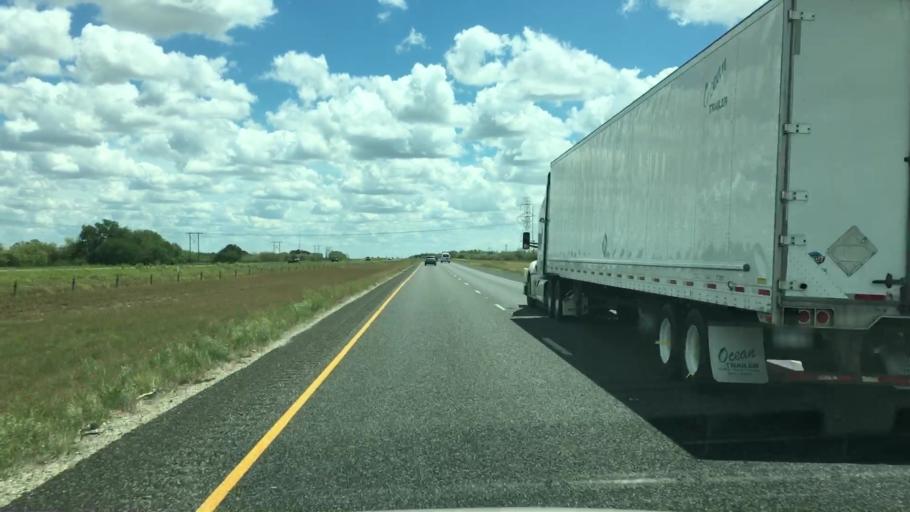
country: US
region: Texas
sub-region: Atascosa County
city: Pleasanton
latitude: 28.8255
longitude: -98.3654
